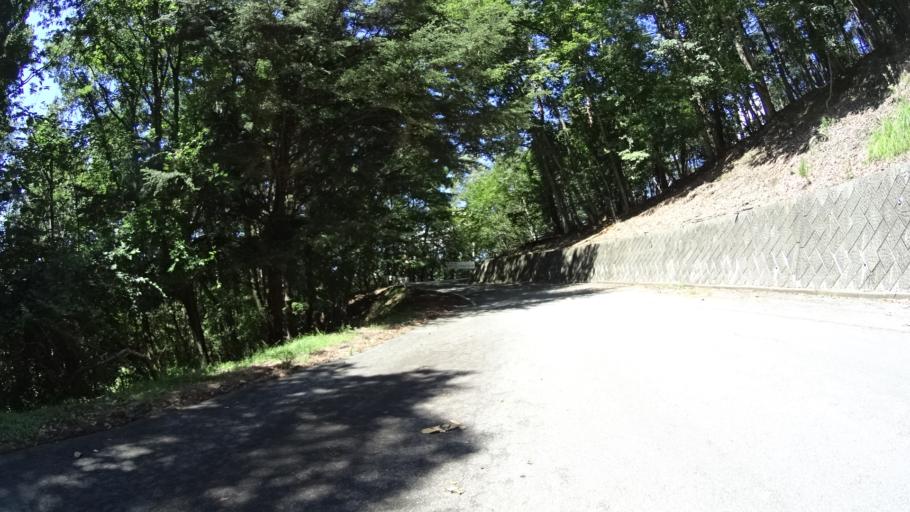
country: JP
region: Yamanashi
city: Enzan
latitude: 35.7418
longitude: 138.8153
